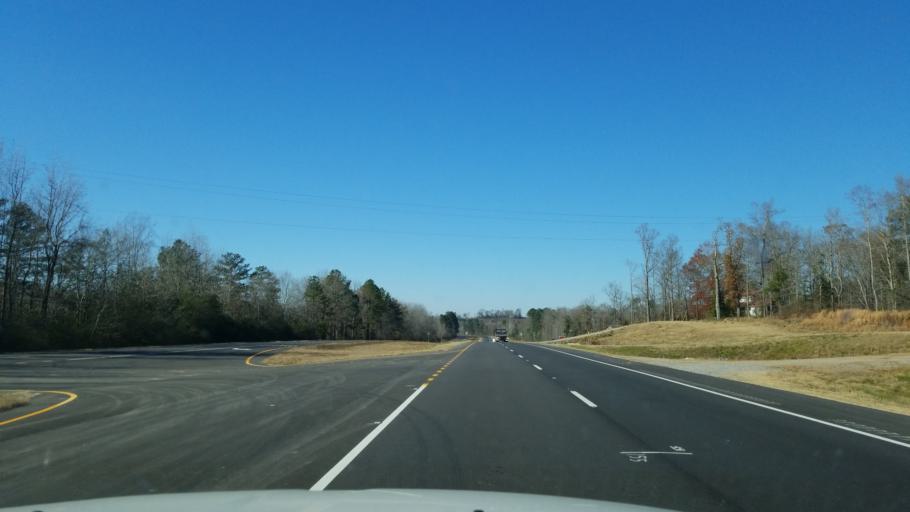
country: US
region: Alabama
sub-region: Pickens County
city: Reform
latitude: 33.3647
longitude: -87.9796
